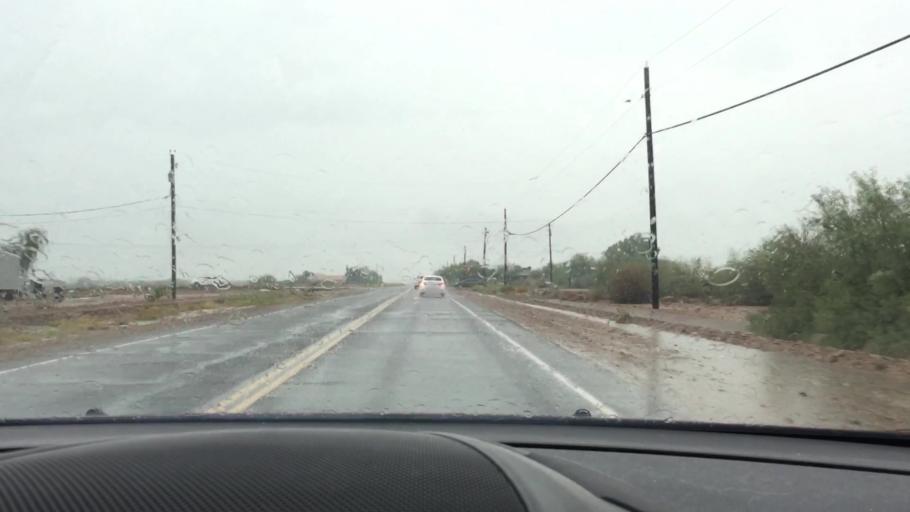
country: US
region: Arizona
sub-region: Maricopa County
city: Scottsdale
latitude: 33.4793
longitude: -111.8827
